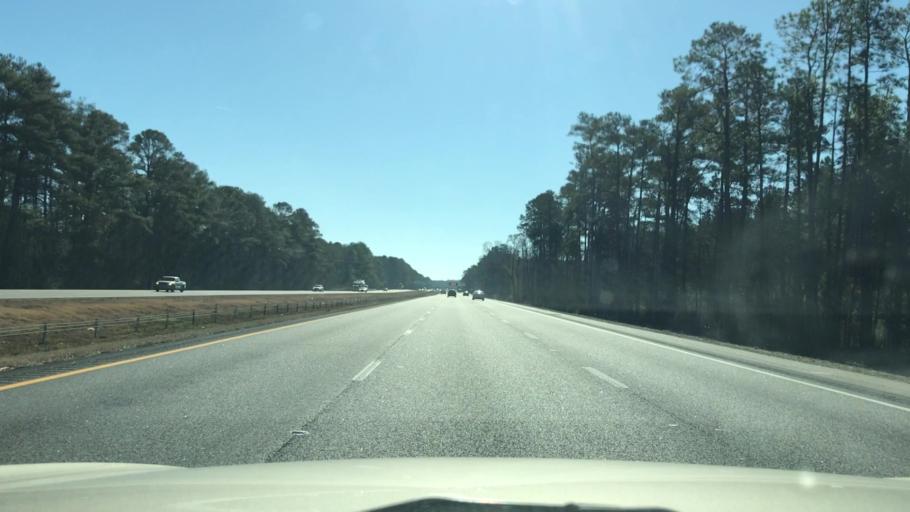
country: US
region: South Carolina
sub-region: Lexington County
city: Pineridge
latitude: 33.9048
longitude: -81.0513
